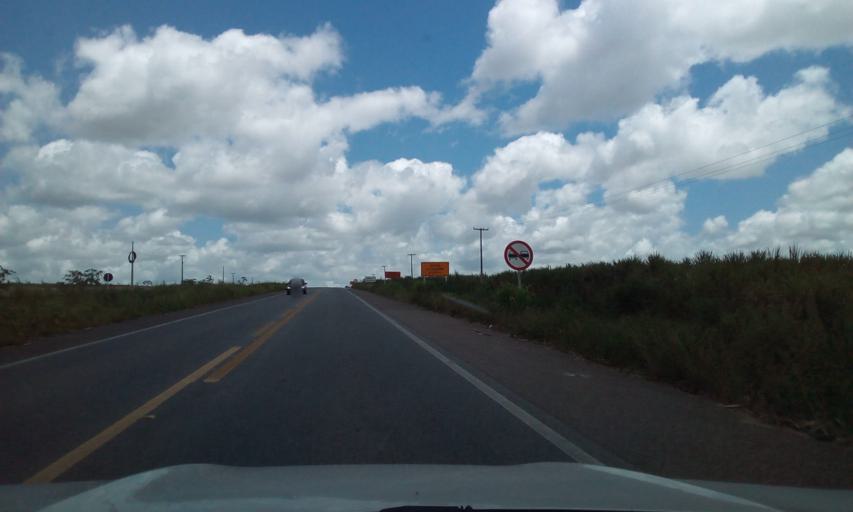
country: BR
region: Alagoas
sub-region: Campo Alegre
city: Campo Alegre
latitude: -9.9018
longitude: -36.3046
